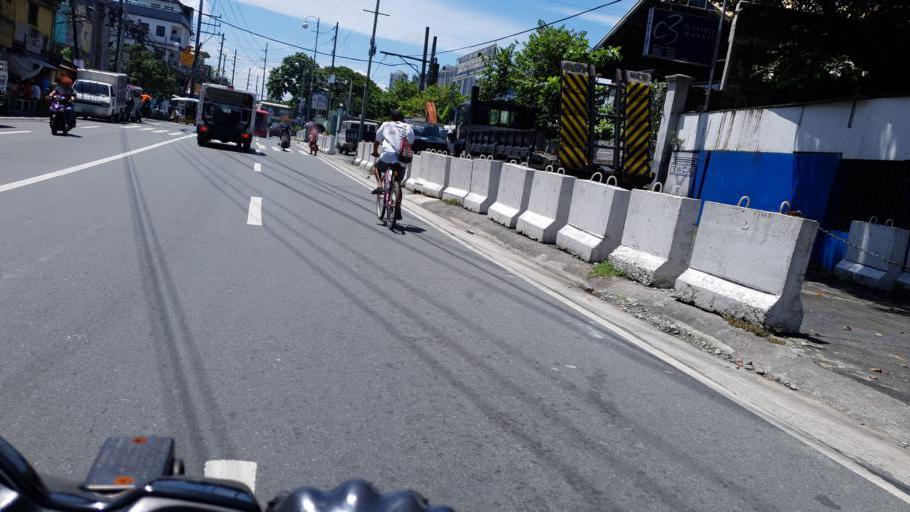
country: PH
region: Metro Manila
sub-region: Pasig
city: Pasig City
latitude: 14.5629
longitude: 121.0600
